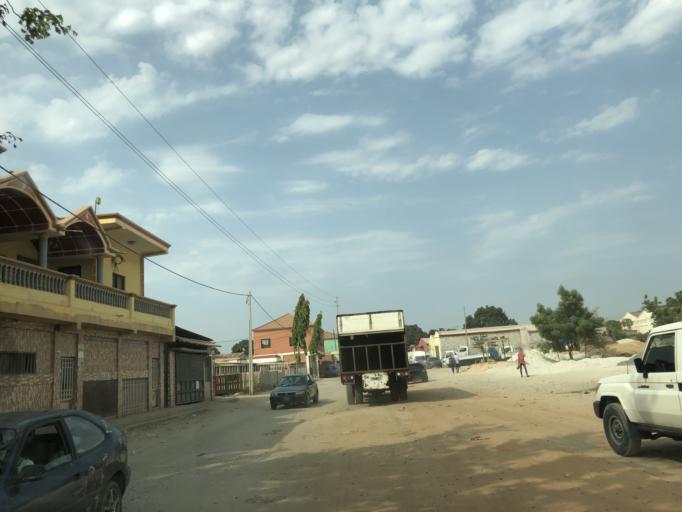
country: AO
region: Luanda
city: Luanda
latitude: -8.8951
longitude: 13.3523
